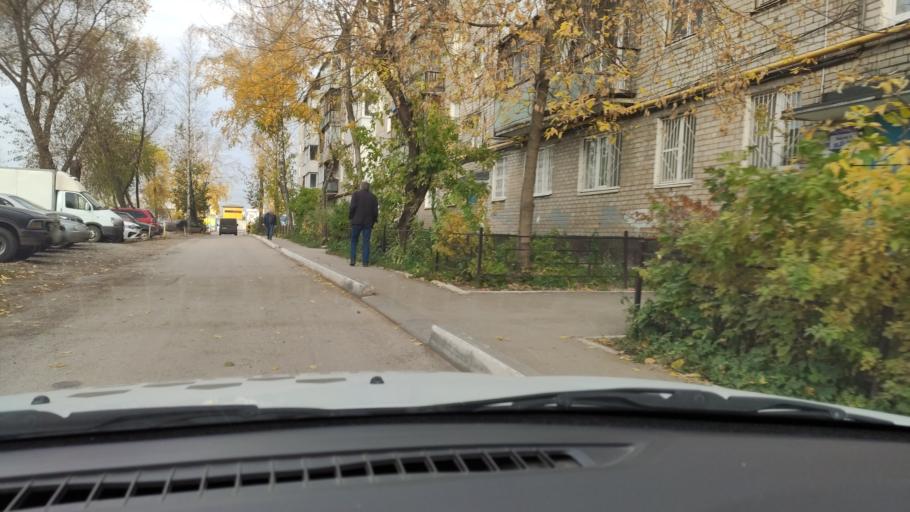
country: RU
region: Perm
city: Perm
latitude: 57.9632
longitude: 56.2217
